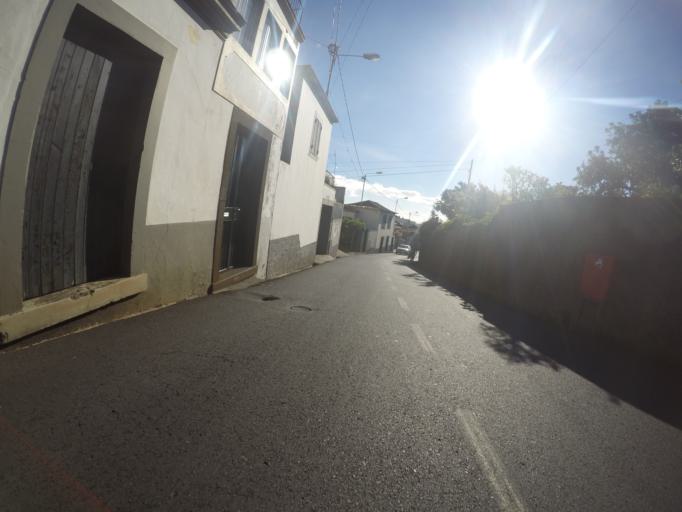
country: PT
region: Madeira
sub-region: Funchal
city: Nossa Senhora do Monte
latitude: 32.6620
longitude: -16.9347
